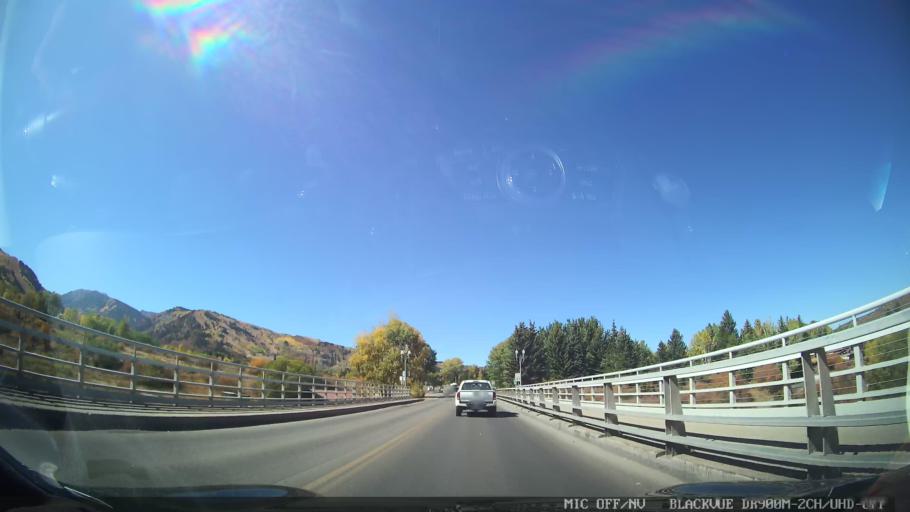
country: US
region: Colorado
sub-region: Pitkin County
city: Aspen
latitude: 39.1953
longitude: -106.8333
